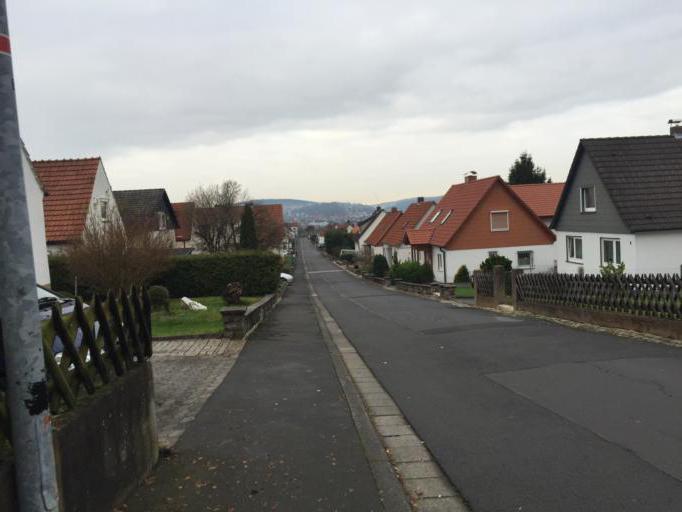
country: DE
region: Hesse
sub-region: Regierungsbezirk Kassel
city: Bad Hersfeld
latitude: 50.8602
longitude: 9.7336
